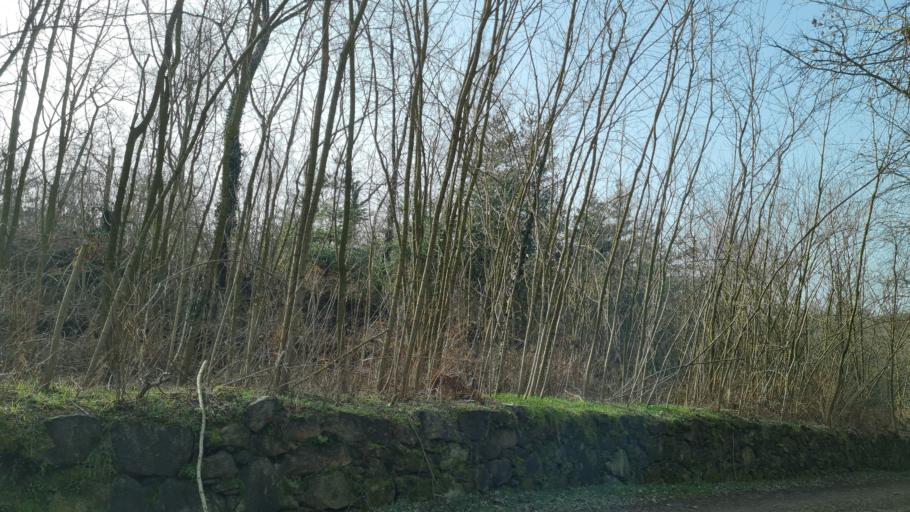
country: IT
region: Piedmont
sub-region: Provincia di Biella
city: Viverone
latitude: 45.4386
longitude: 8.0531
